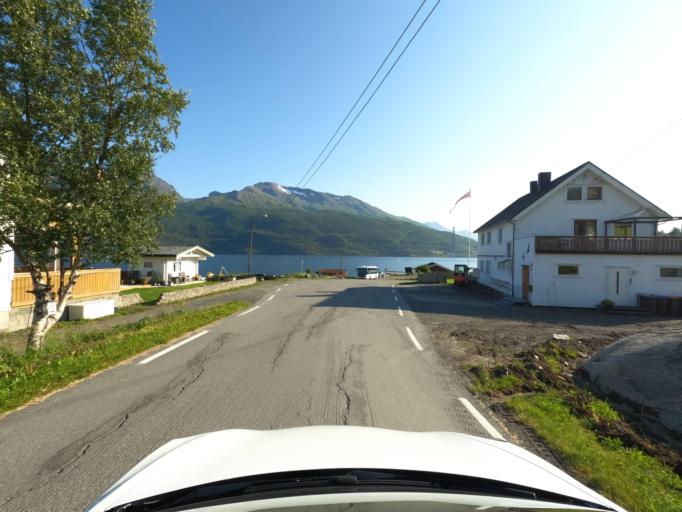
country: NO
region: Nordland
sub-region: Narvik
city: Narvik
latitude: 68.4705
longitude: 17.5042
